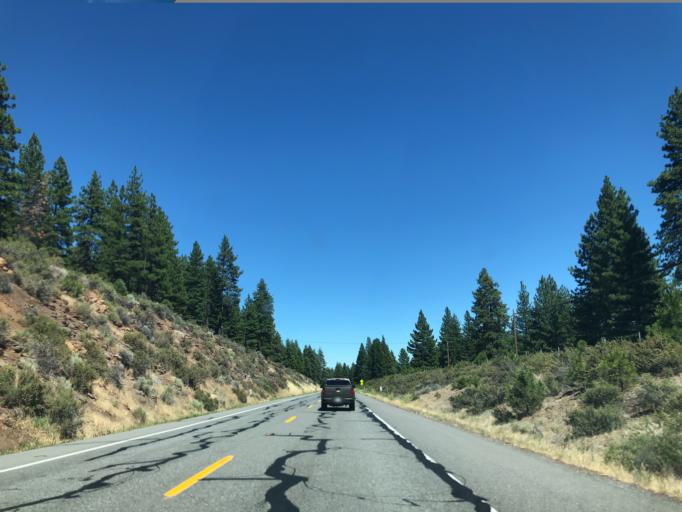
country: US
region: California
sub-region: Lassen County
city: Susanville
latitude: 40.4149
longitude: -120.7319
